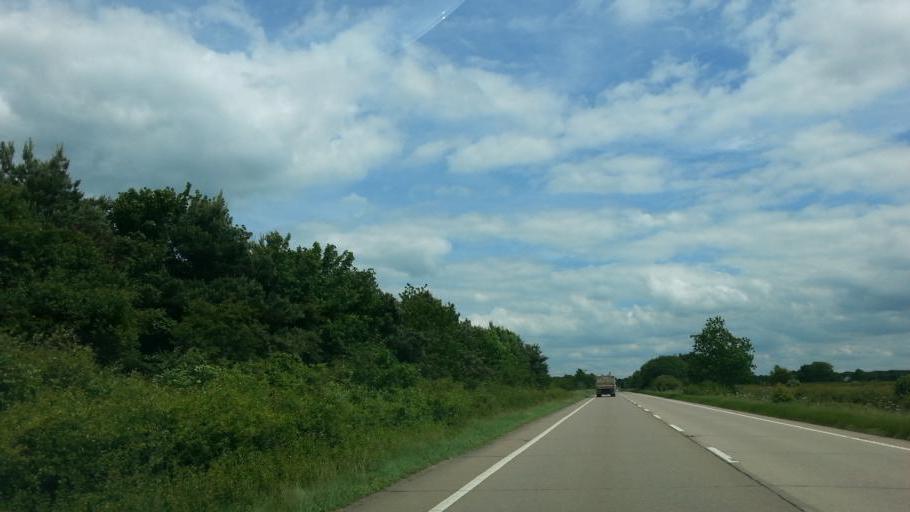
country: GB
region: England
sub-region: Lincolnshire
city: Long Bennington
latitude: 52.9350
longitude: -0.7853
